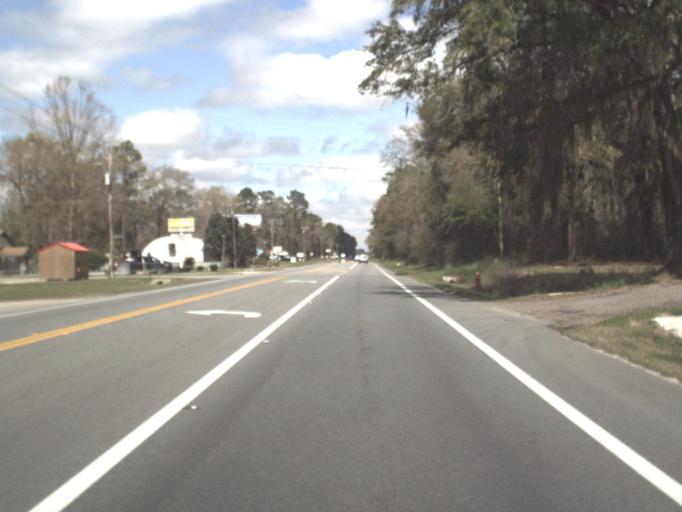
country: US
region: Florida
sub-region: Wakulla County
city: Crawfordville
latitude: 30.2377
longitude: -84.3624
